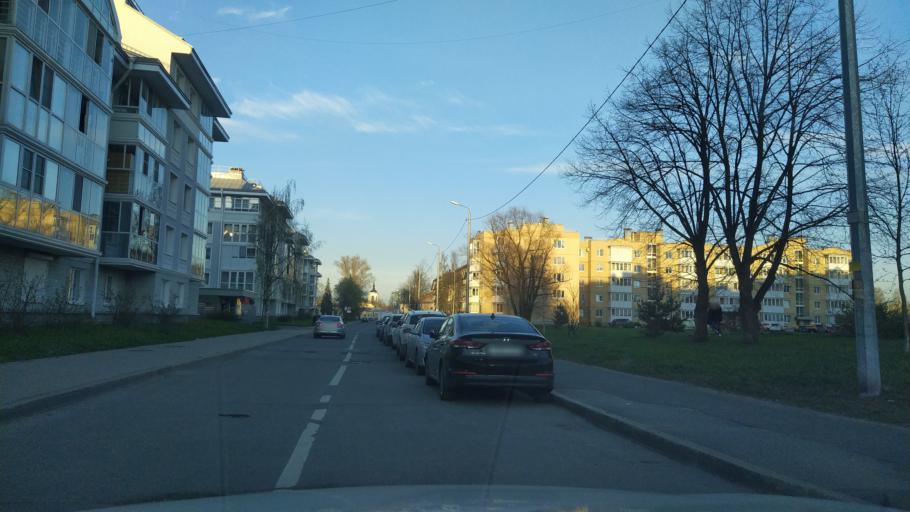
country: RU
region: St.-Petersburg
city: Pushkin
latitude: 59.7072
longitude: 30.3850
